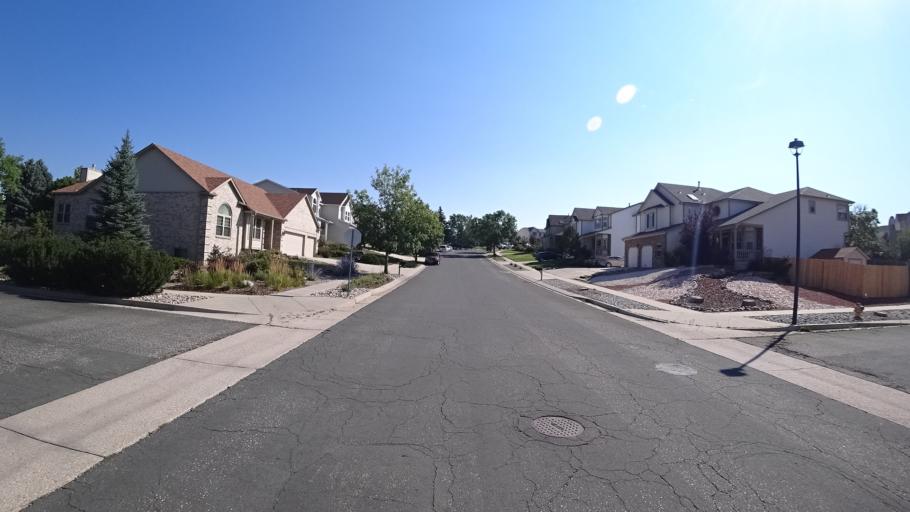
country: US
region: Colorado
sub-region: El Paso County
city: Air Force Academy
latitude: 38.9545
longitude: -104.7826
